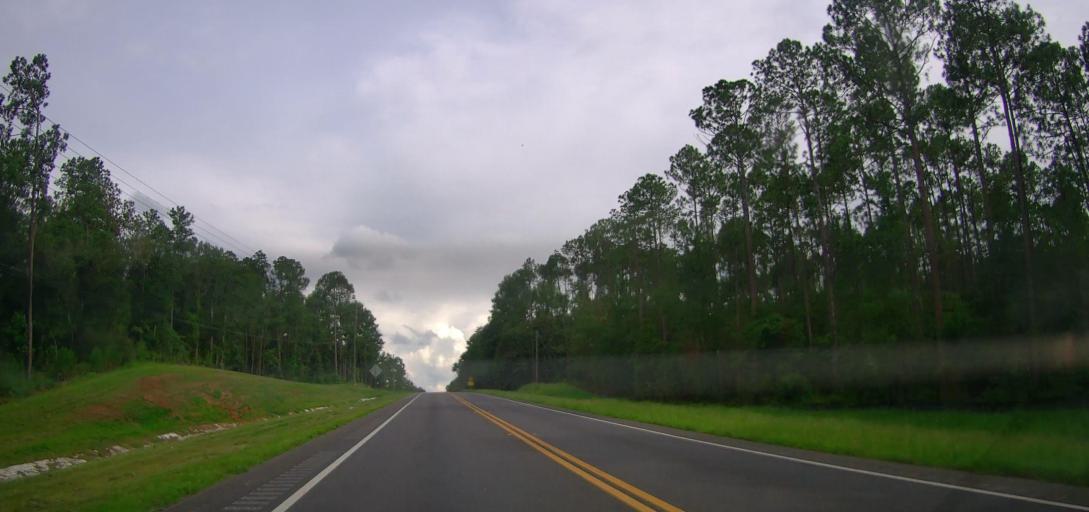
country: US
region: Georgia
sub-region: Wayne County
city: Jesup
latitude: 31.6666
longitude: -81.9171
